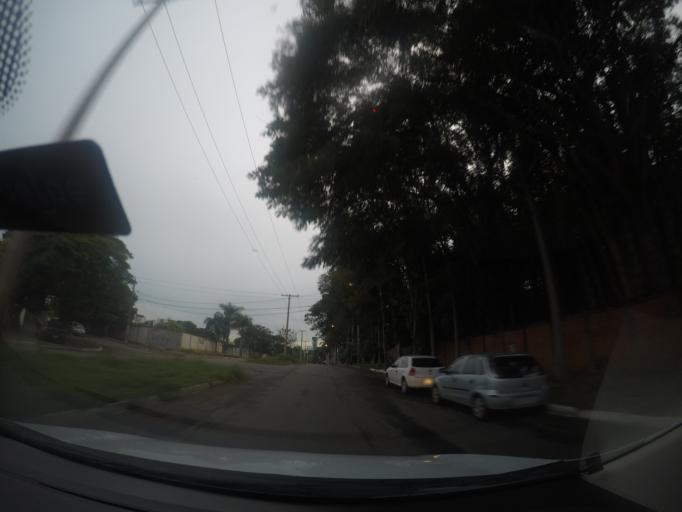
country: BR
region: Goias
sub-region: Goiania
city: Goiania
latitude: -16.6385
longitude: -49.2454
